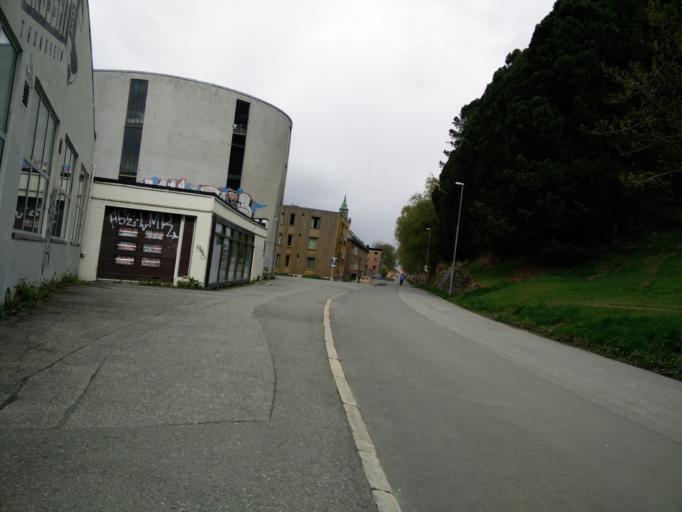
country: NO
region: Sor-Trondelag
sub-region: Trondheim
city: Trondheim
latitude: 63.4188
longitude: 10.3974
